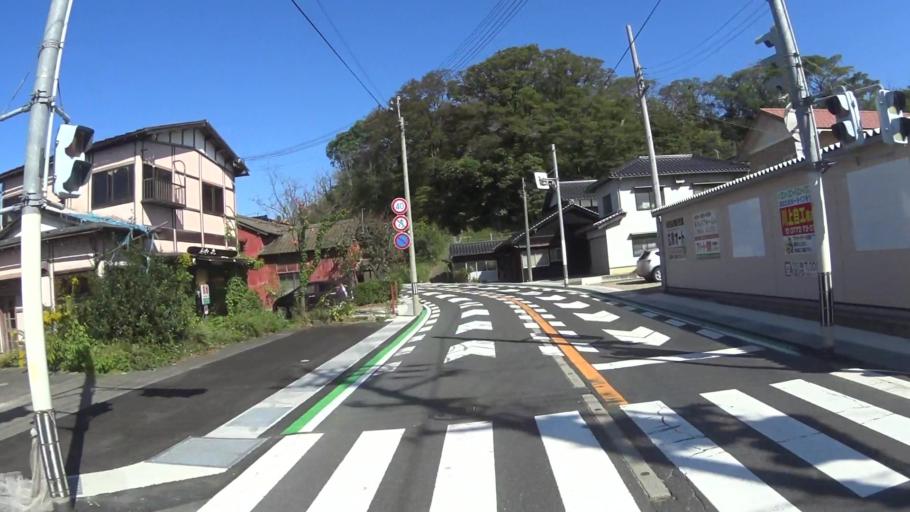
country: JP
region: Kyoto
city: Miyazu
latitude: 35.6818
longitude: 135.0304
